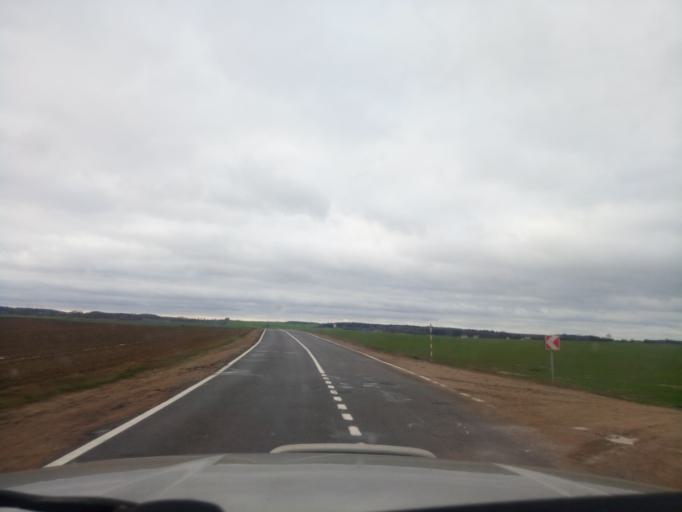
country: BY
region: Minsk
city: Kapyl'
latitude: 53.1983
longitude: 27.2034
